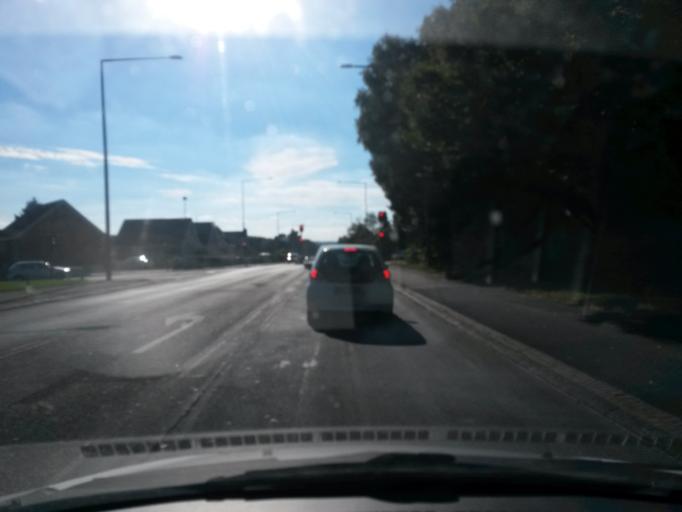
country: DK
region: Central Jutland
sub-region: Silkeborg Kommune
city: Silkeborg
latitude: 56.1781
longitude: 9.5305
